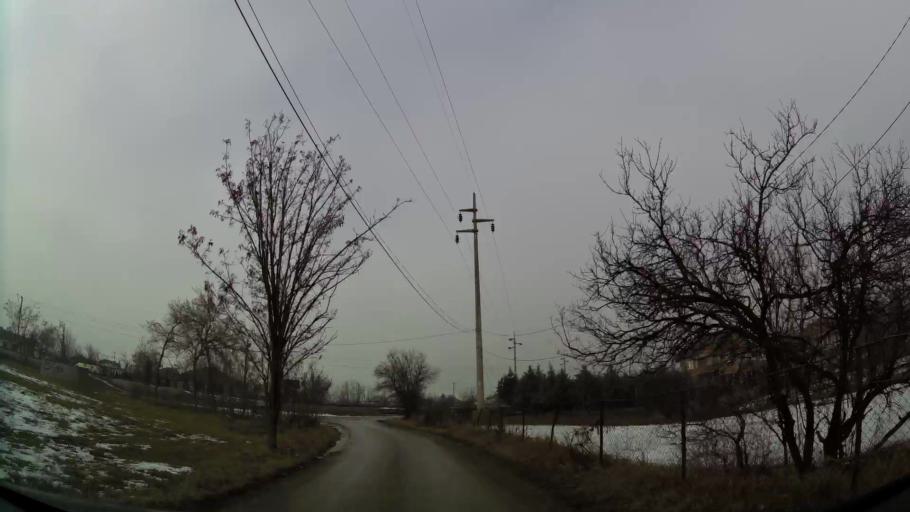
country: MK
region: Ilinden
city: Ilinden
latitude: 41.9965
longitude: 21.5616
